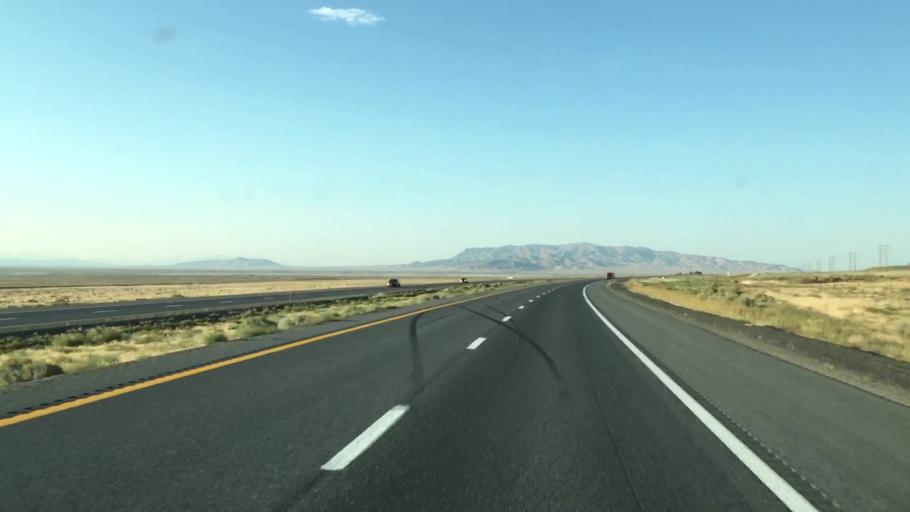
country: US
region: Nevada
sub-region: Pershing County
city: Lovelock
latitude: 40.5581
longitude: -118.2764
